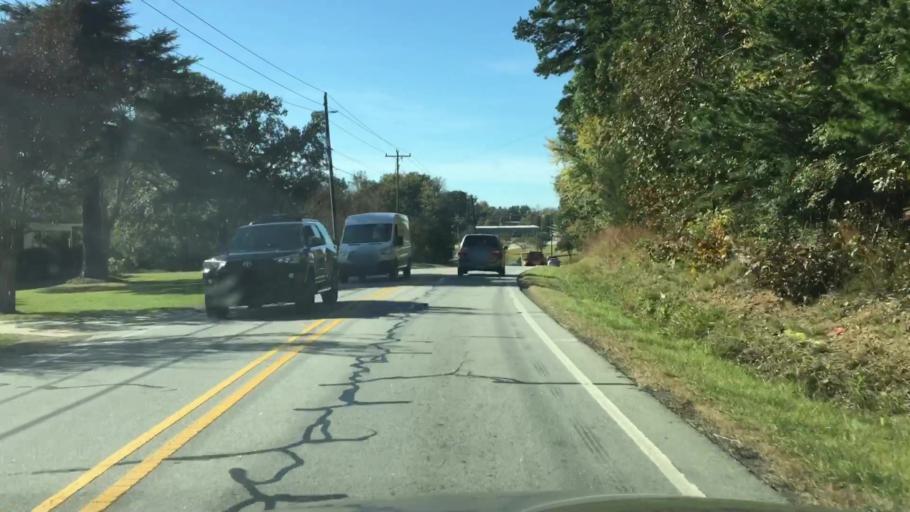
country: US
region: North Carolina
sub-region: Rowan County
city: Salisbury
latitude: 35.6639
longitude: -80.5210
